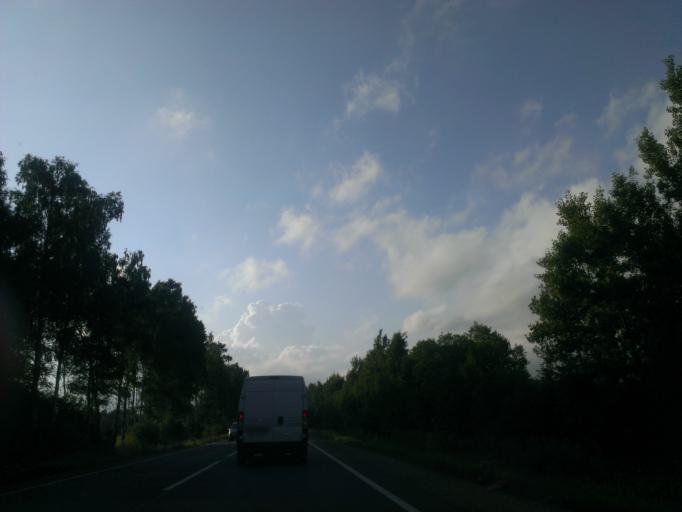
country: LV
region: Kekava
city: Balozi
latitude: 56.8742
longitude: 24.1691
